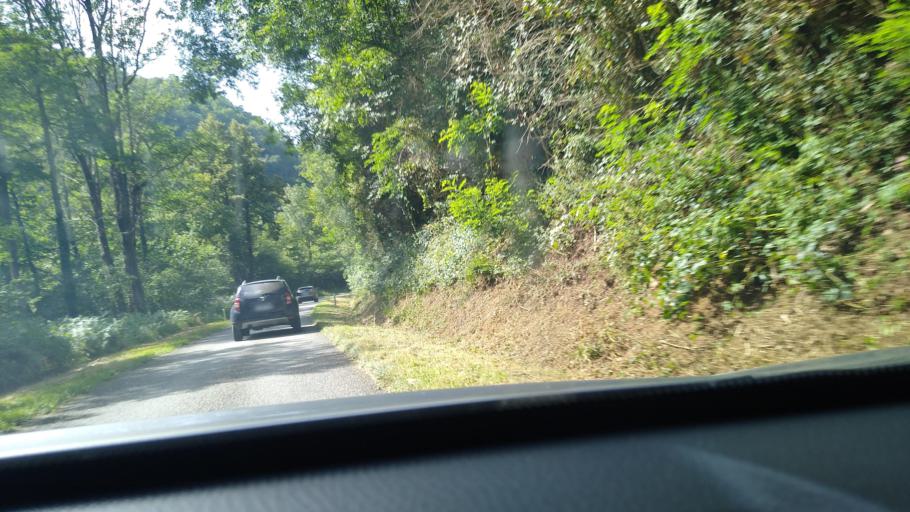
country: FR
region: Midi-Pyrenees
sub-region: Departement de l'Ariege
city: Saint-Girons
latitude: 42.9126
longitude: 1.2073
